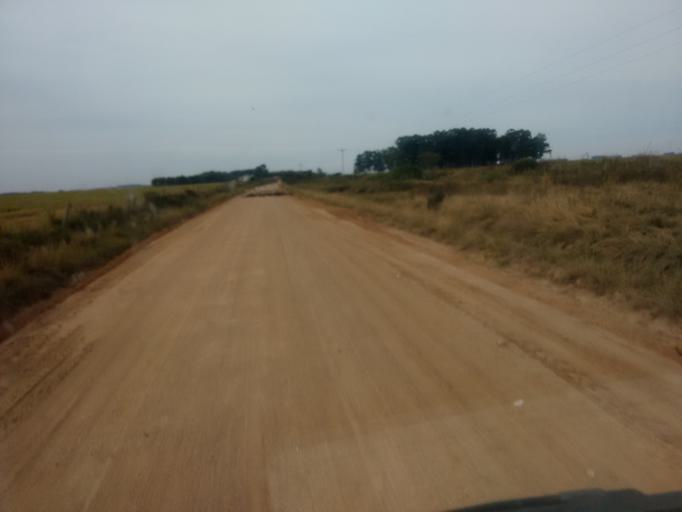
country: BR
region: Rio Grande do Sul
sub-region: Camaqua
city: Camaqua
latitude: -31.1224
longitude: -51.7610
